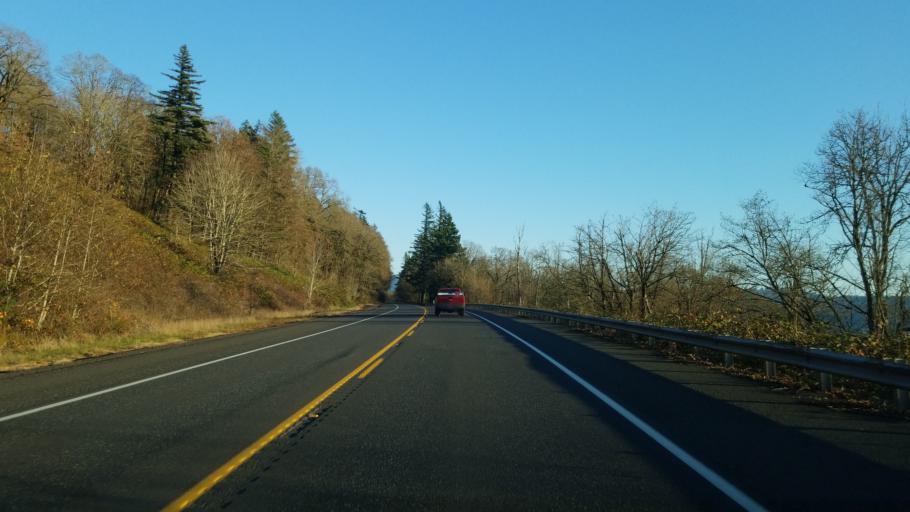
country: US
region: Washington
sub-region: Clark County
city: Washougal
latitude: 45.5696
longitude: -122.2931
